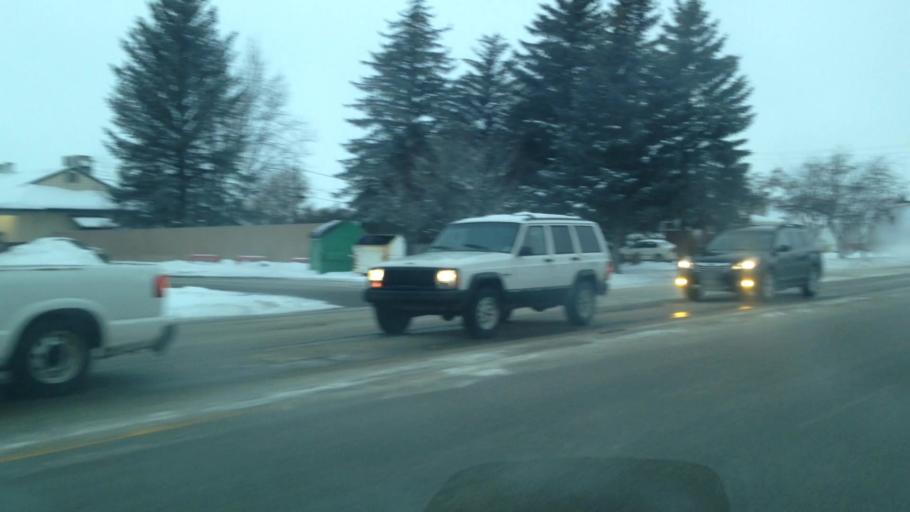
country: US
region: Idaho
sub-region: Madison County
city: Rexburg
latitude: 43.8283
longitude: -111.7782
